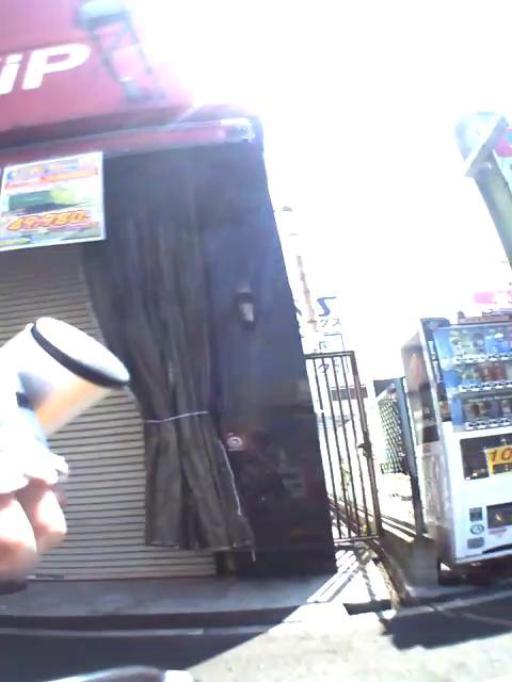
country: JP
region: Osaka
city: Osaka-shi
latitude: 34.6611
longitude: 135.5047
